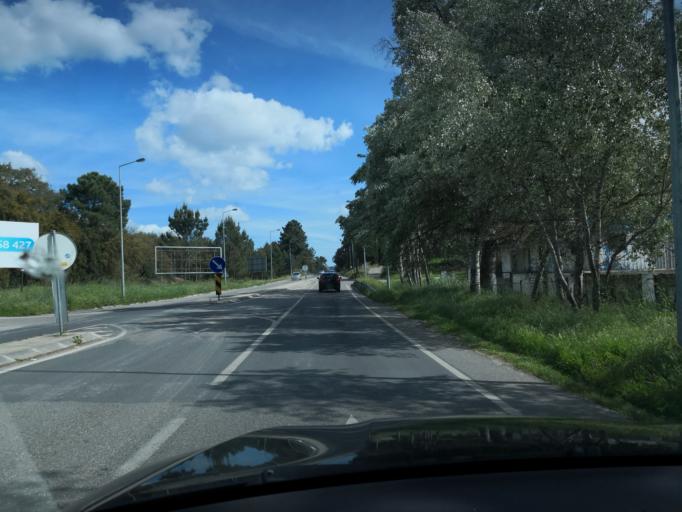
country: PT
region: Setubal
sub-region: Barreiro
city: Santo Antonio da Charneca
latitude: 38.5535
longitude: -9.0343
